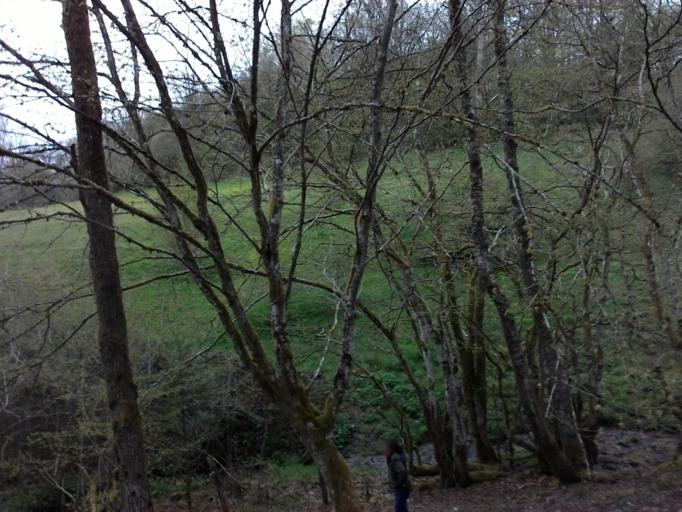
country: FR
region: Bourgogne
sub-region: Departement de la Cote-d'Or
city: Saulieu
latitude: 47.2435
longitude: 4.0629
